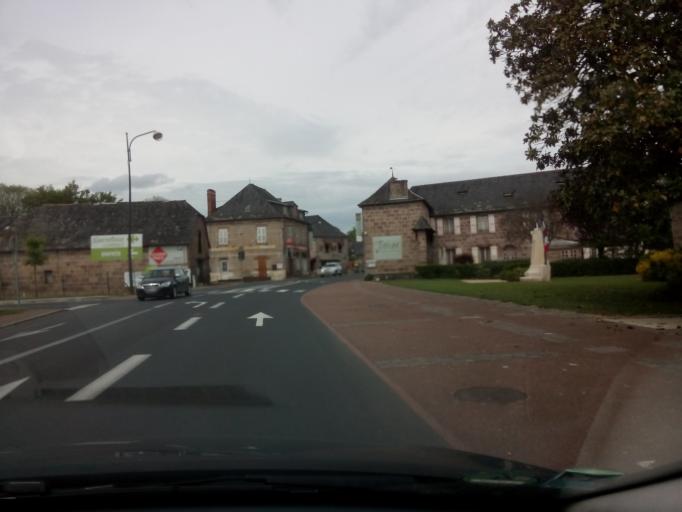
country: FR
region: Limousin
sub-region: Departement de la Correze
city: Varetz
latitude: 45.1929
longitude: 1.4512
